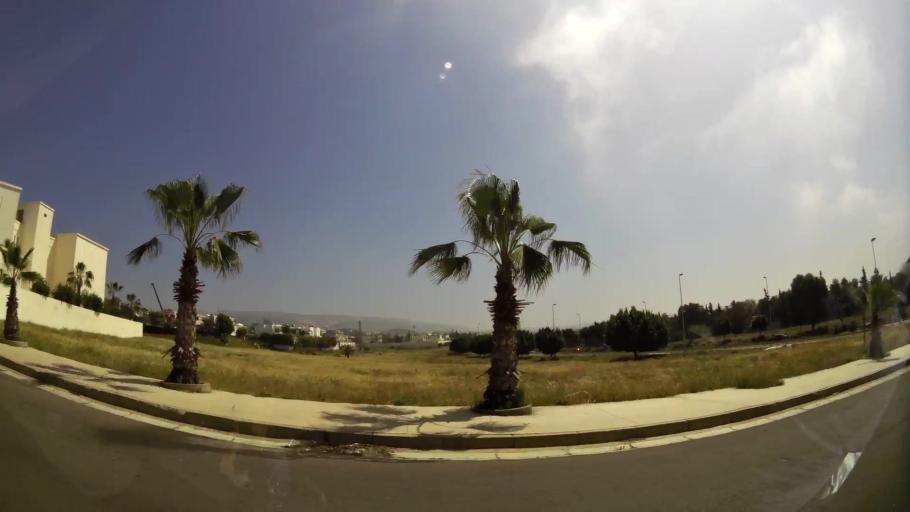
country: MA
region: Souss-Massa-Draa
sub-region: Agadir-Ida-ou-Tnan
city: Agadir
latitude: 30.4374
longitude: -9.5971
